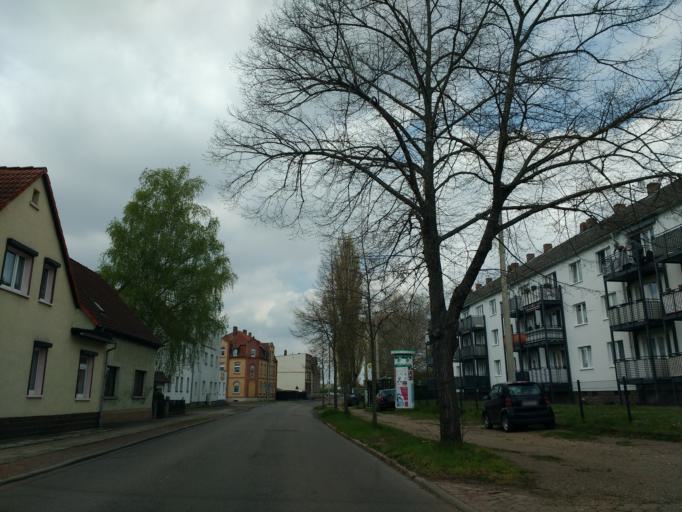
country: DE
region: Saxony-Anhalt
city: Dieskau
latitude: 51.4568
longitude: 12.0317
